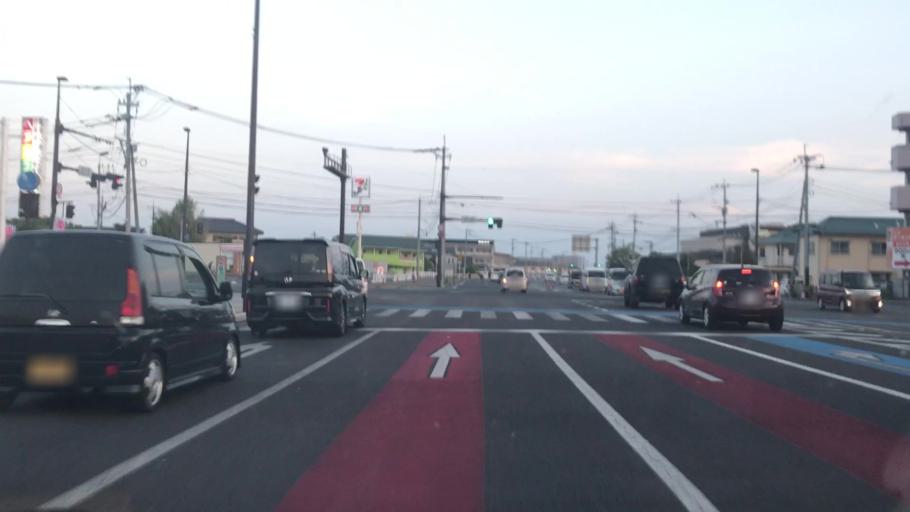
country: JP
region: Saga Prefecture
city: Saga-shi
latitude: 33.2397
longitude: 130.2945
